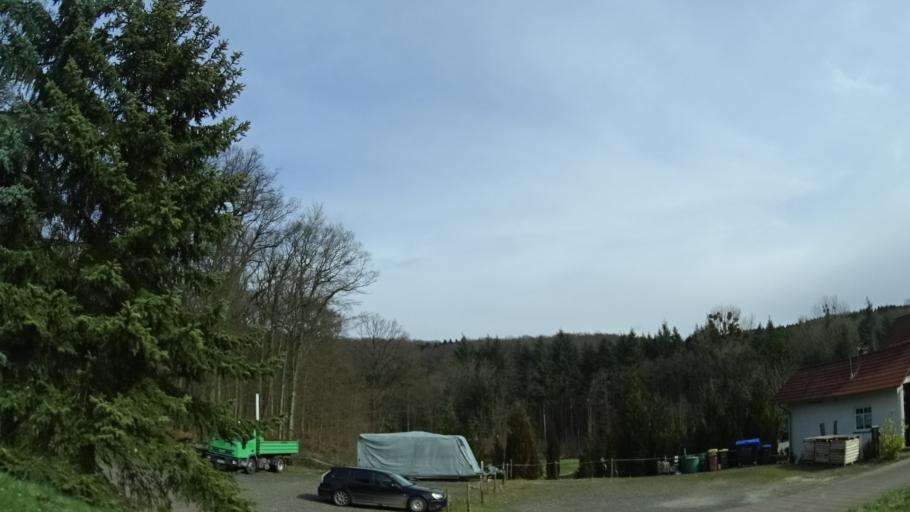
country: DE
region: Rheinland-Pfalz
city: Munchwald
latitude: 49.9020
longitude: 7.6787
